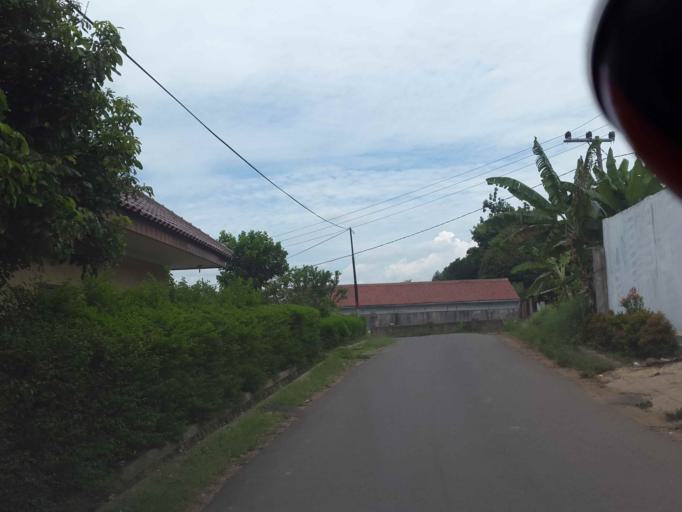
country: ID
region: Lampung
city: Kedaton
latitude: -5.3559
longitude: 105.2212
